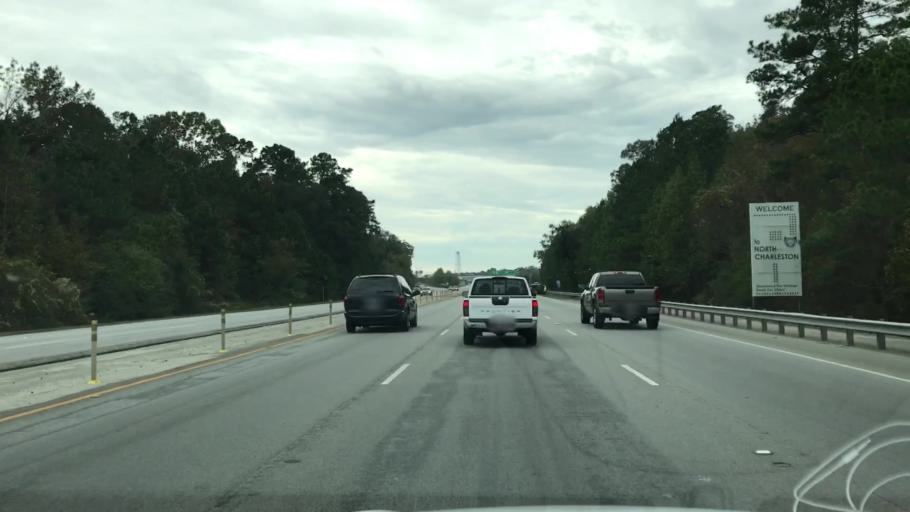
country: US
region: South Carolina
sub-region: Berkeley County
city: Goose Creek
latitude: 32.9817
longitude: -80.0427
